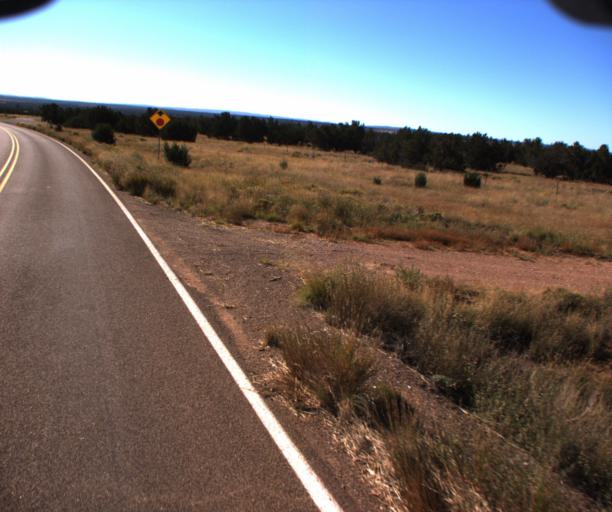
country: US
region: Arizona
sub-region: Navajo County
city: Heber-Overgaard
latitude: 34.4828
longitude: -110.3401
